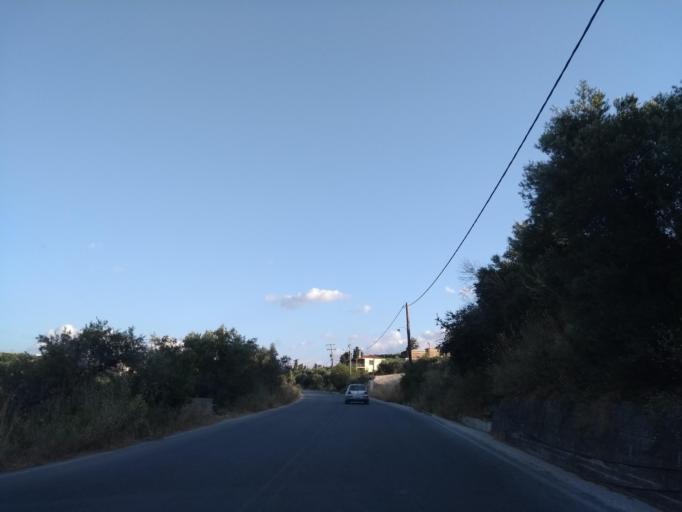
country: GR
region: Crete
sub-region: Nomos Chanias
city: Kalivai
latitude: 35.4406
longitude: 24.1754
